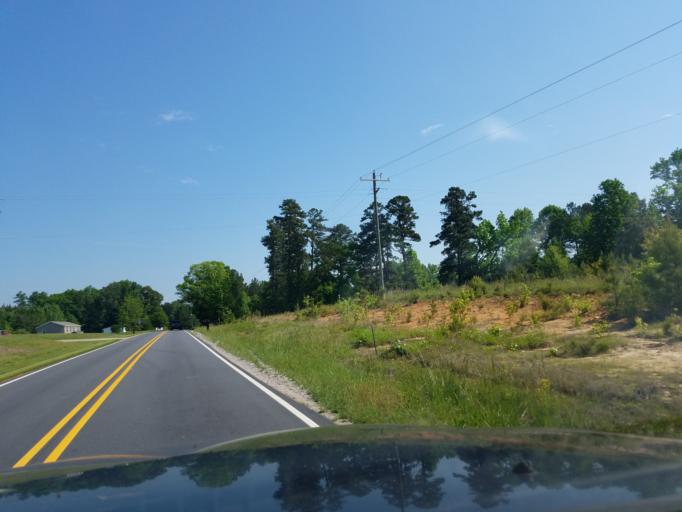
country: US
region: North Carolina
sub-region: Vance County
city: Henderson
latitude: 36.3564
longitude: -78.4547
